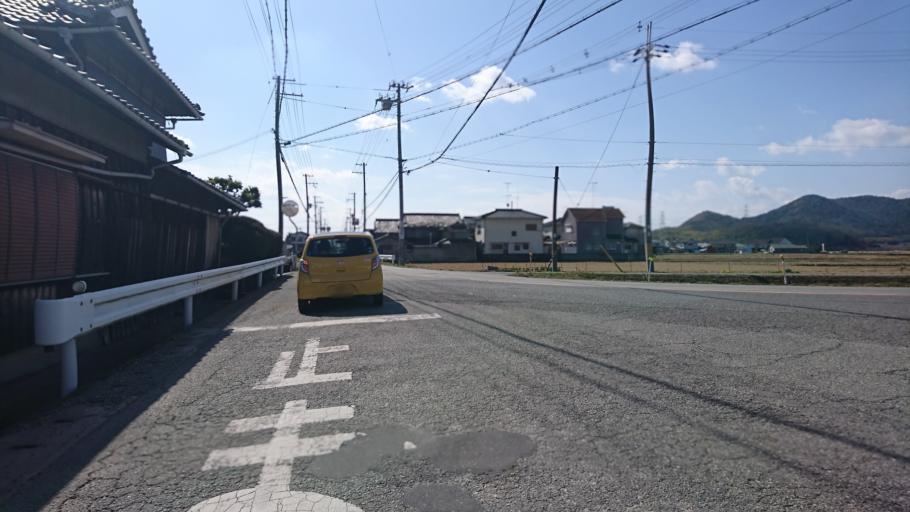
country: JP
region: Hyogo
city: Kakogawacho-honmachi
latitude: 34.8085
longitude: 134.8190
